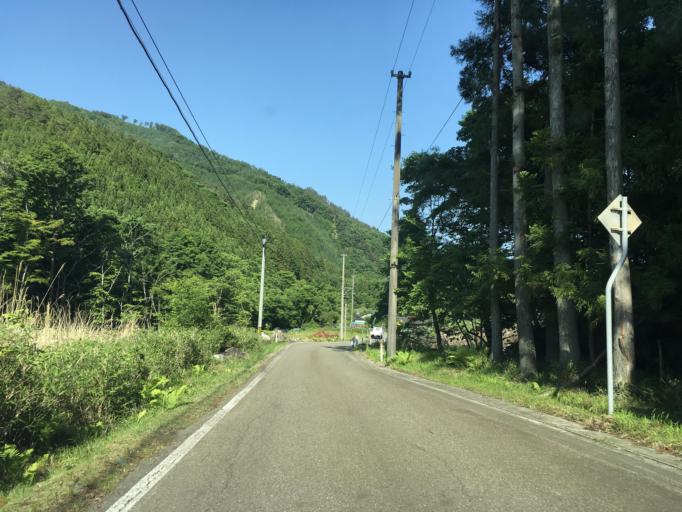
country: JP
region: Iwate
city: Kamaishi
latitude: 39.1977
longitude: 141.8281
